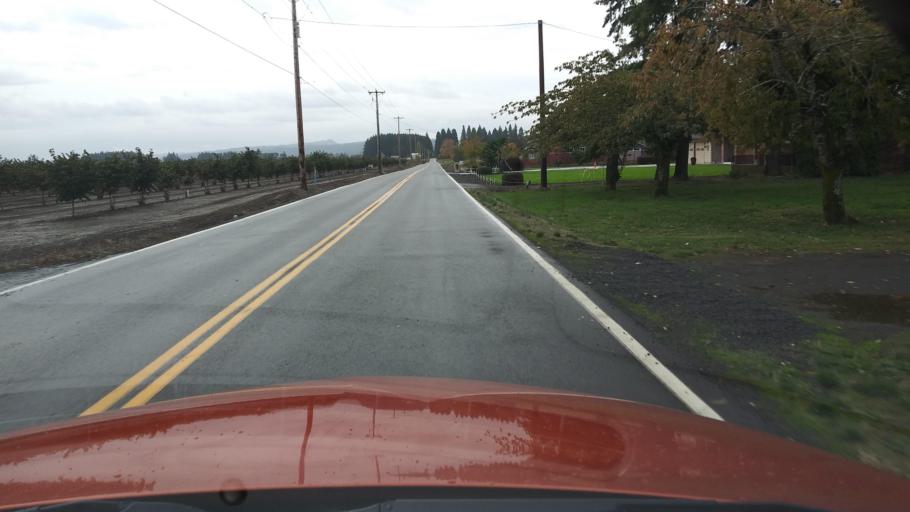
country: US
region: Oregon
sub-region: Washington County
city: Forest Grove
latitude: 45.5488
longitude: -123.0870
